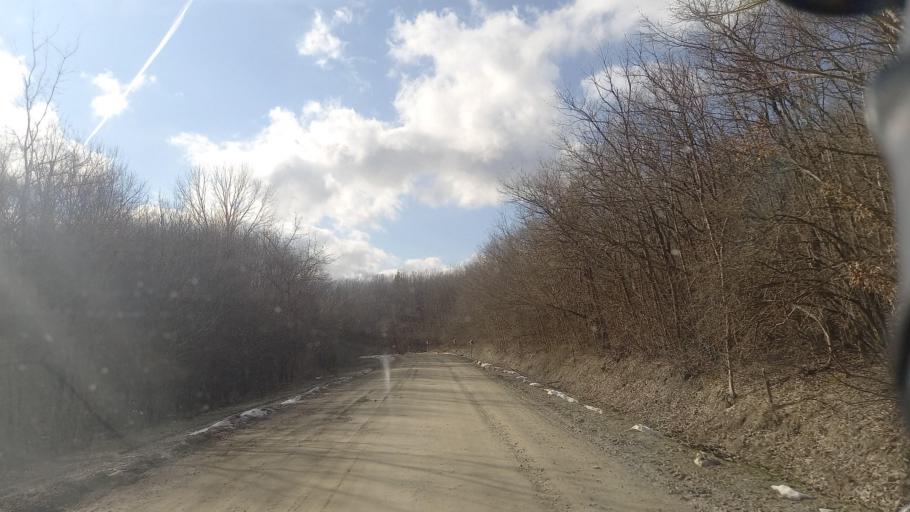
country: RU
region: Krasnodarskiy
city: Smolenskaya
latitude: 44.5957
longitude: 38.8268
